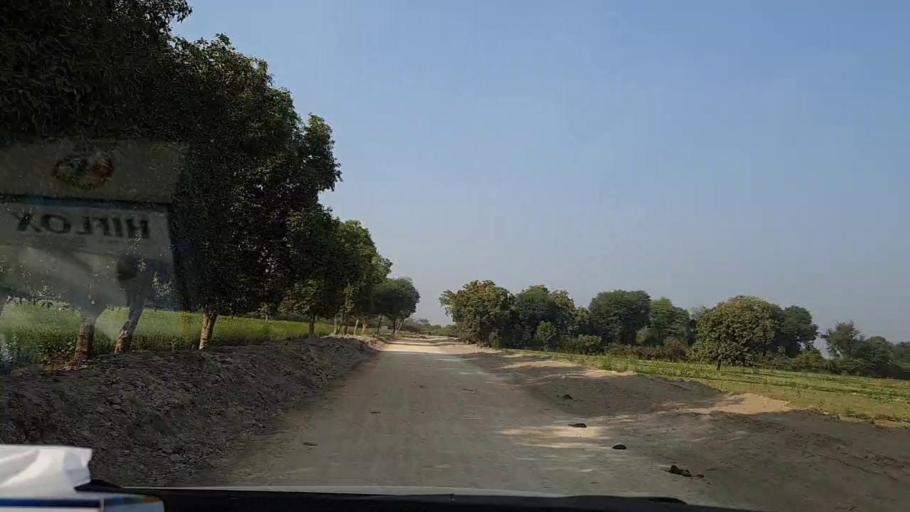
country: PK
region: Sindh
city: Tando Ghulam Ali
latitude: 25.1473
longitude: 68.8763
